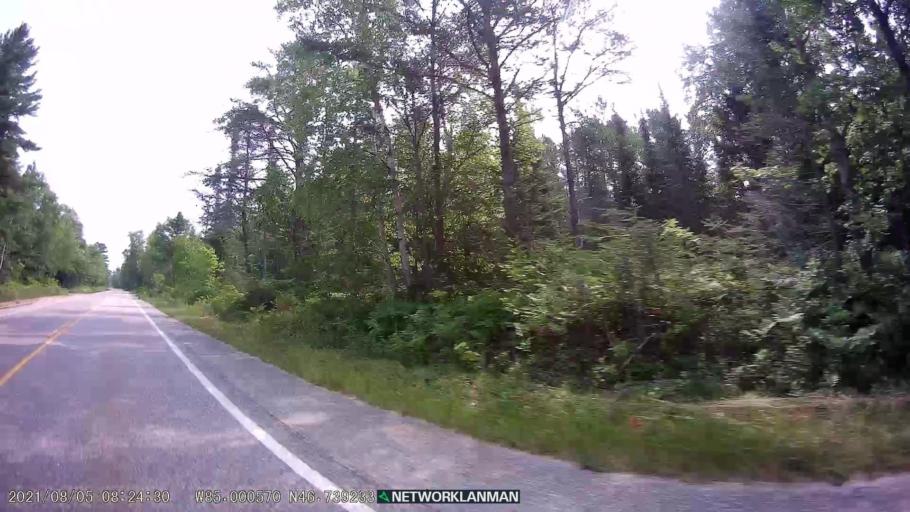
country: US
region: Michigan
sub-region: Luce County
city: Newberry
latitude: 46.7394
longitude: -85.0002
